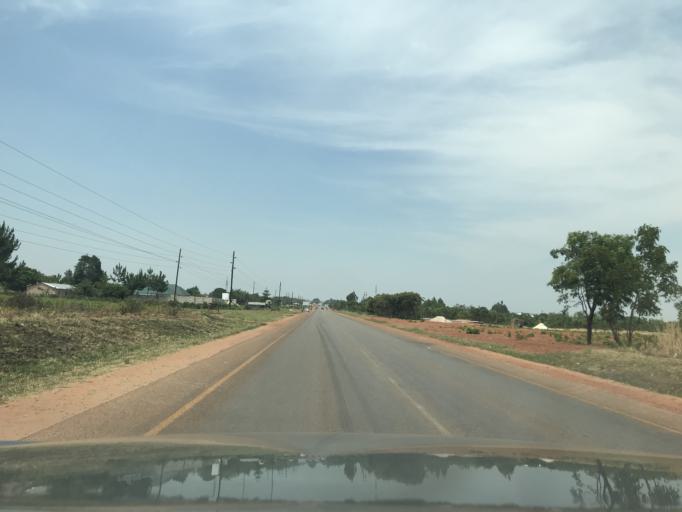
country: ZM
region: Northern
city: Kasama
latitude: -10.2121
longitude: 31.1599
